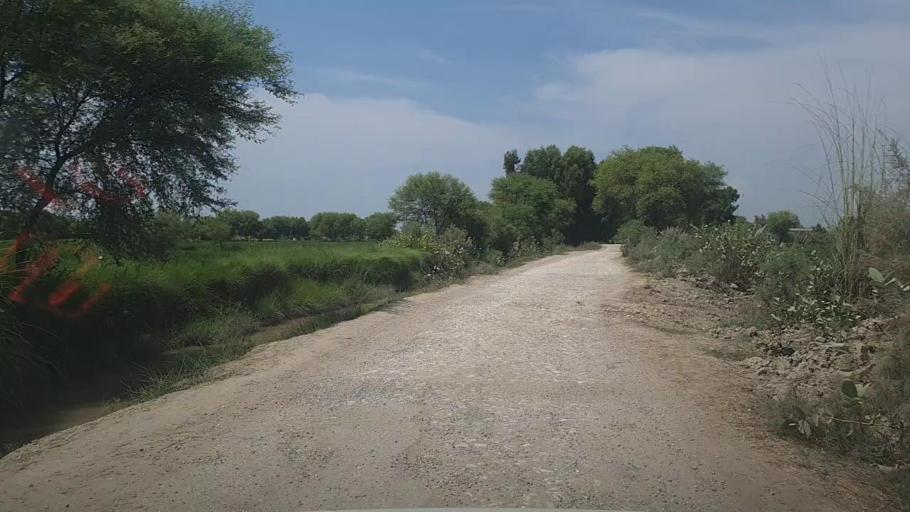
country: PK
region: Sindh
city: Kandhkot
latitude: 28.2759
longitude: 69.2359
